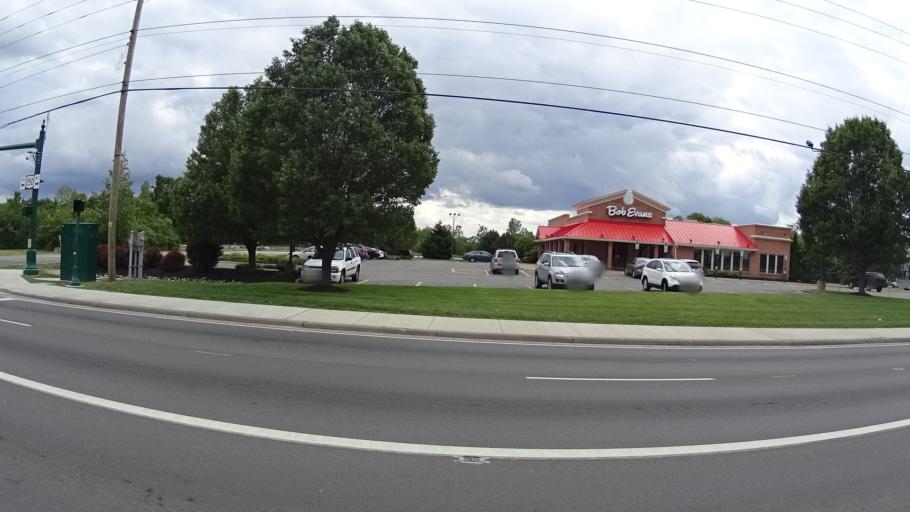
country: US
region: Ohio
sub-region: Erie County
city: Sandusky
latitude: 41.4154
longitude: -82.6712
